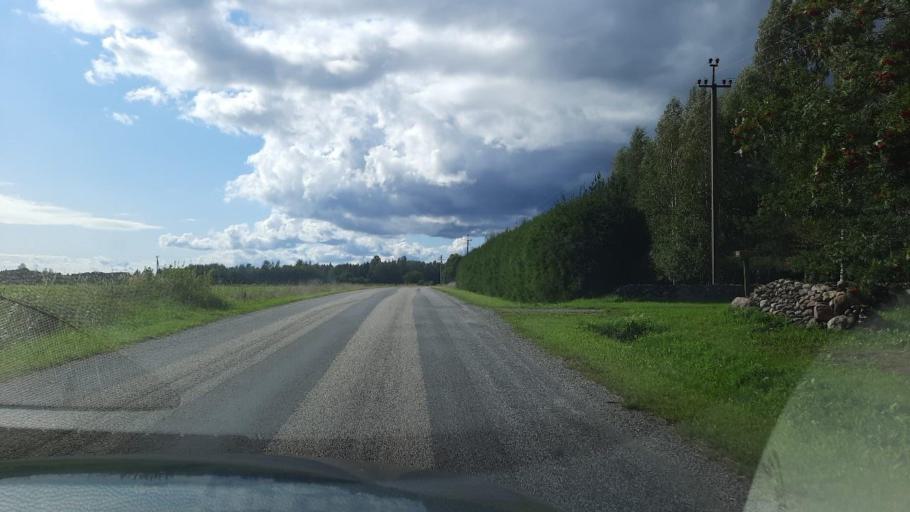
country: EE
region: Paernumaa
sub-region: Tootsi vald
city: Tootsi
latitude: 58.4830
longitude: 24.9045
